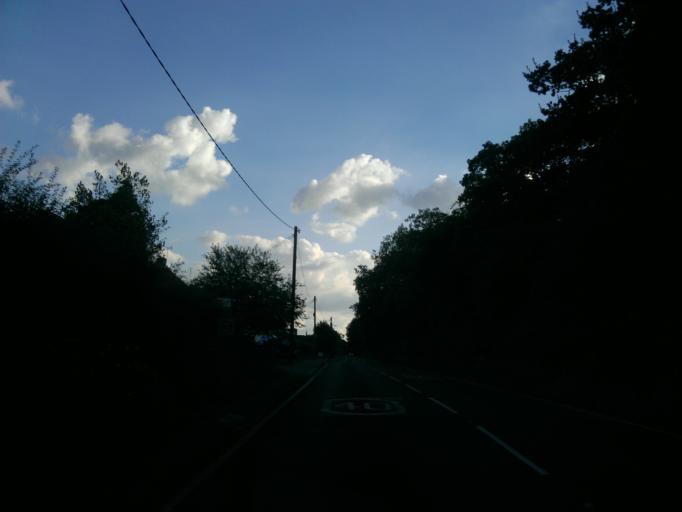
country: GB
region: England
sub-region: Essex
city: Sible Hedingham
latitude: 51.9287
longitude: 0.5933
